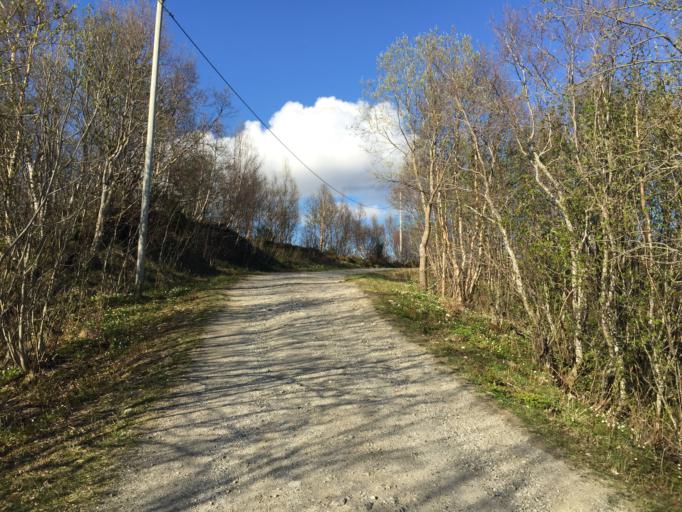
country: NO
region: Nordland
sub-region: Bodo
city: Lopsmarka
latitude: 67.2956
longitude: 14.5569
